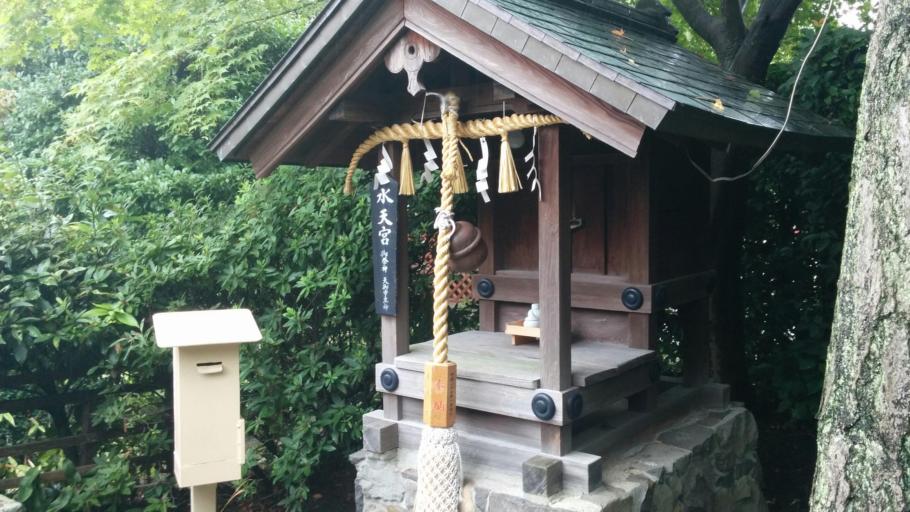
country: JP
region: Osaka
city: Takaishi
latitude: 34.5021
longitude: 135.4973
